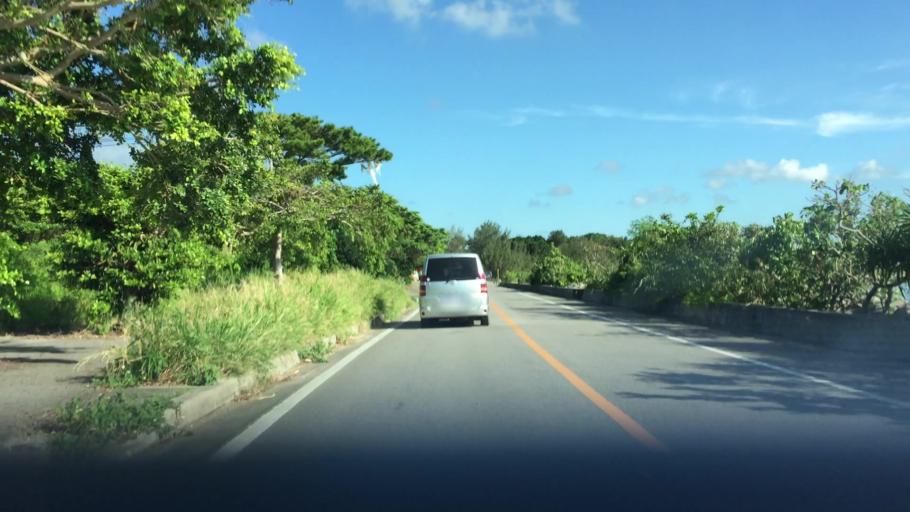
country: JP
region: Okinawa
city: Ishigaki
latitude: 24.4204
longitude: 124.1336
